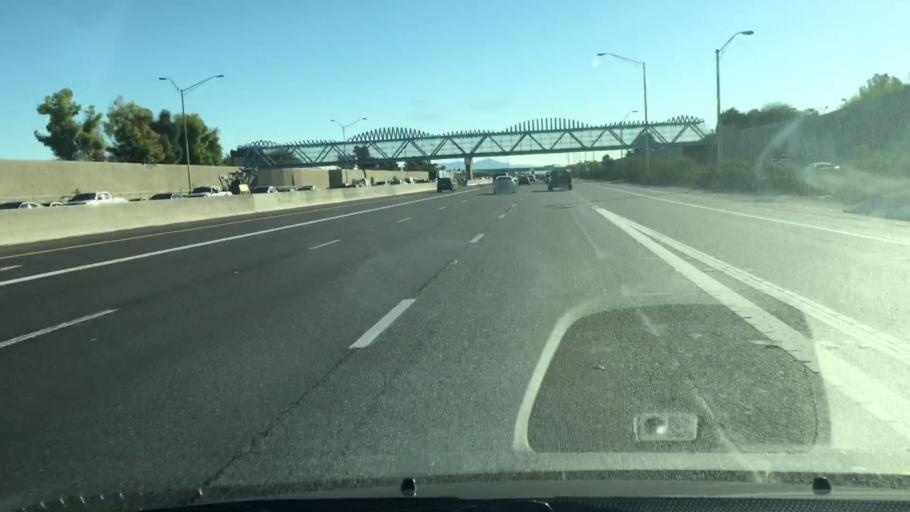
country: US
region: Arizona
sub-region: Maricopa County
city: Tempe
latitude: 33.3855
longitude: -111.9027
